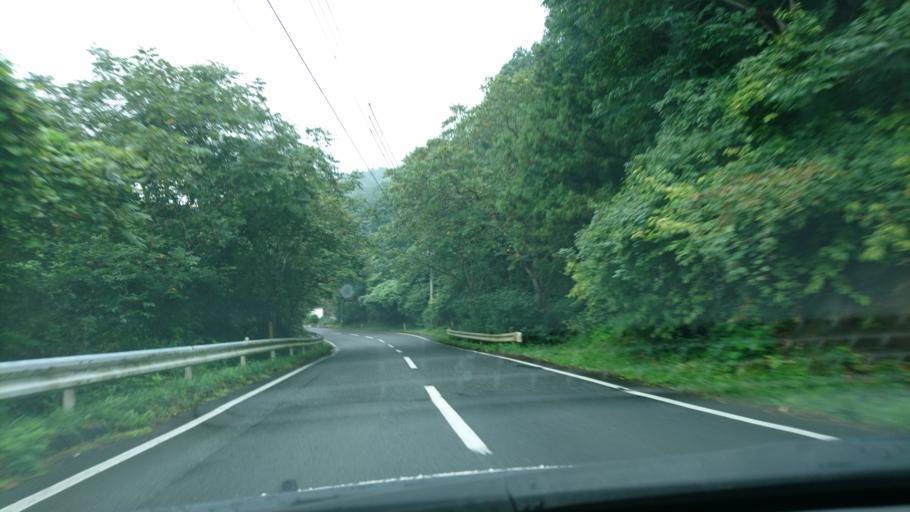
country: JP
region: Iwate
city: Ichinoseki
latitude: 38.8930
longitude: 141.2666
